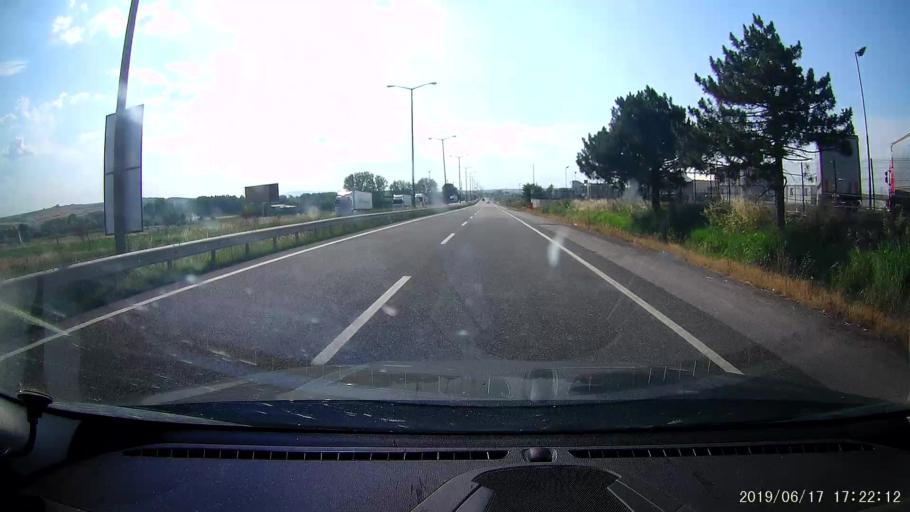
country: GR
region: East Macedonia and Thrace
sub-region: Nomos Evrou
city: Rizia
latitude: 41.7103
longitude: 26.3793
